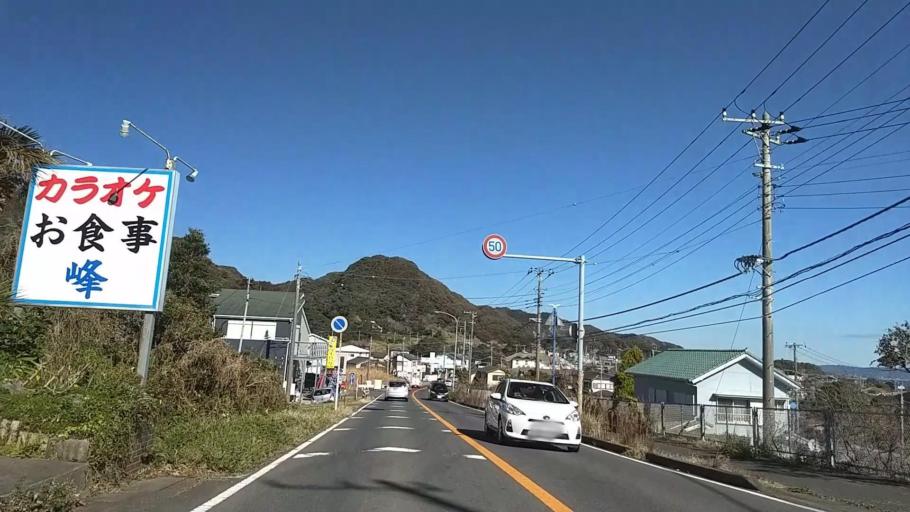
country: JP
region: Chiba
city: Kawaguchi
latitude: 35.0612
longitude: 140.0733
